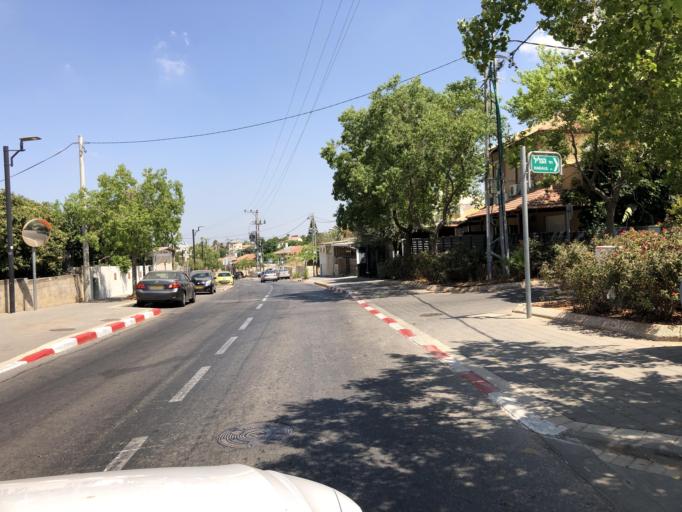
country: IL
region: Central District
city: Rosh Ha'Ayin
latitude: 32.0976
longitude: 34.9569
